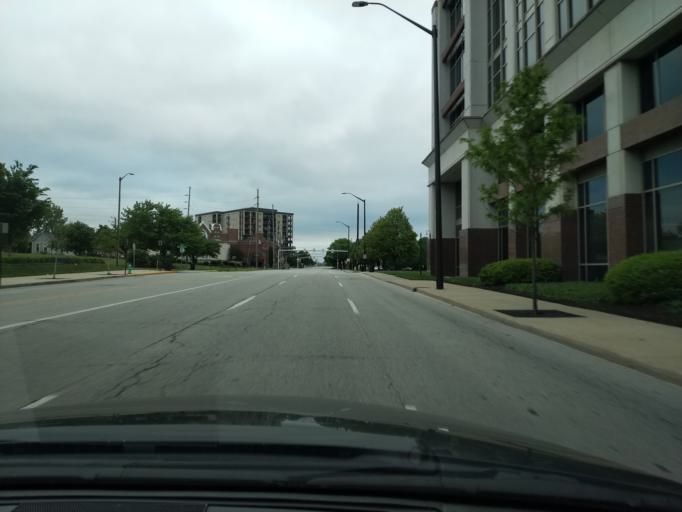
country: US
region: Indiana
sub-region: Marion County
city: Indianapolis
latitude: 39.7632
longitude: -86.1493
